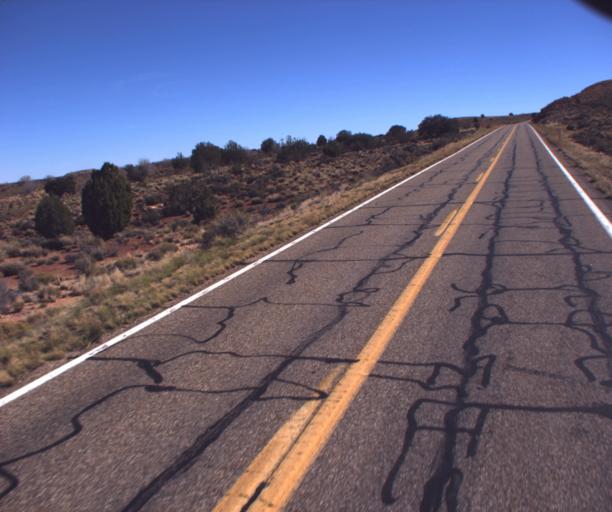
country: US
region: Arizona
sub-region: Coconino County
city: Fredonia
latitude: 36.9074
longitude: -112.4017
